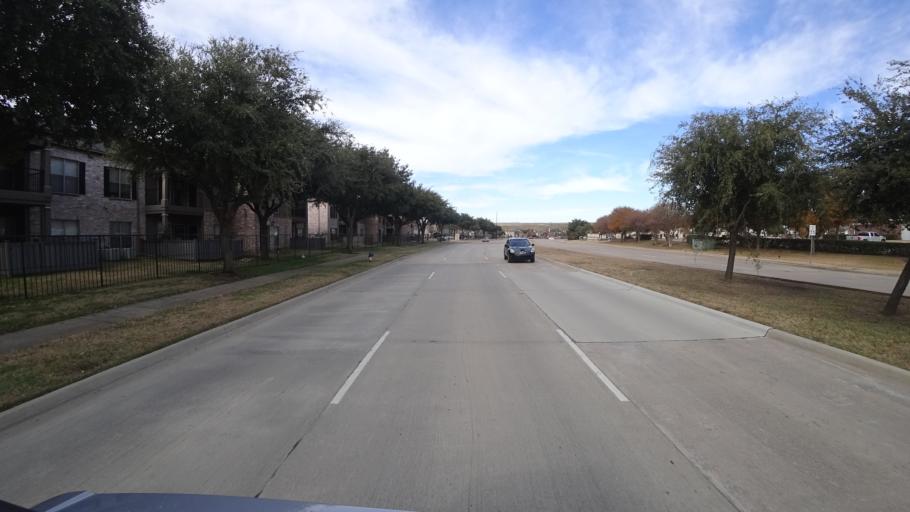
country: US
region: Texas
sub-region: Denton County
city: Lewisville
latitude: 33.0128
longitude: -96.9443
